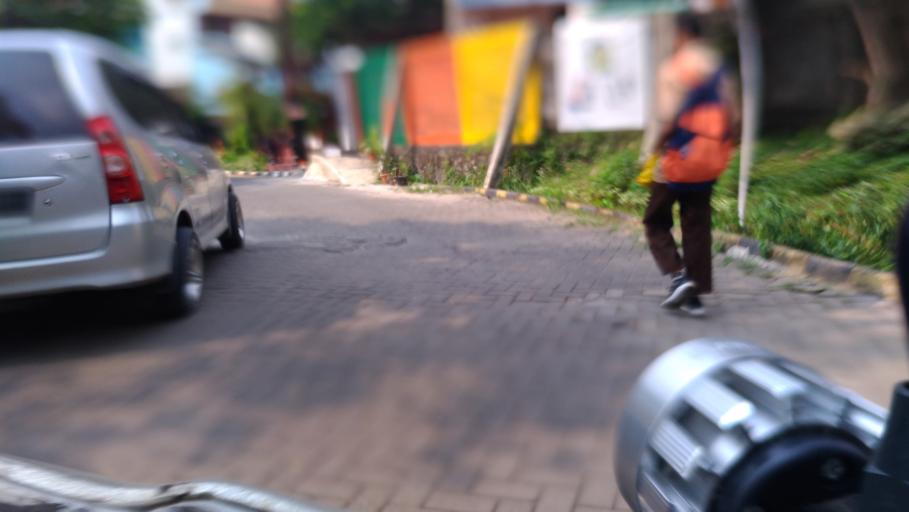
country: ID
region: West Java
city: Depok
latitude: -6.3702
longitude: 106.8777
